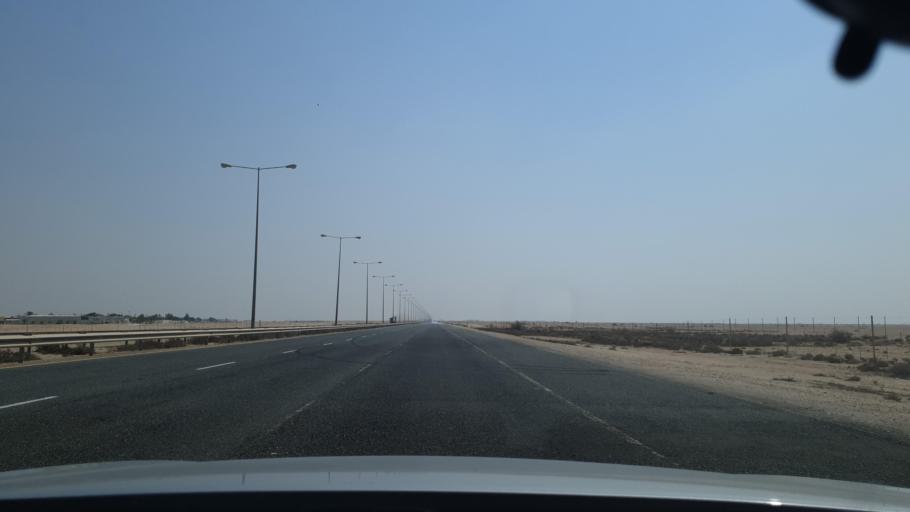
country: QA
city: Al Ghuwayriyah
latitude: 25.8162
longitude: 51.3698
